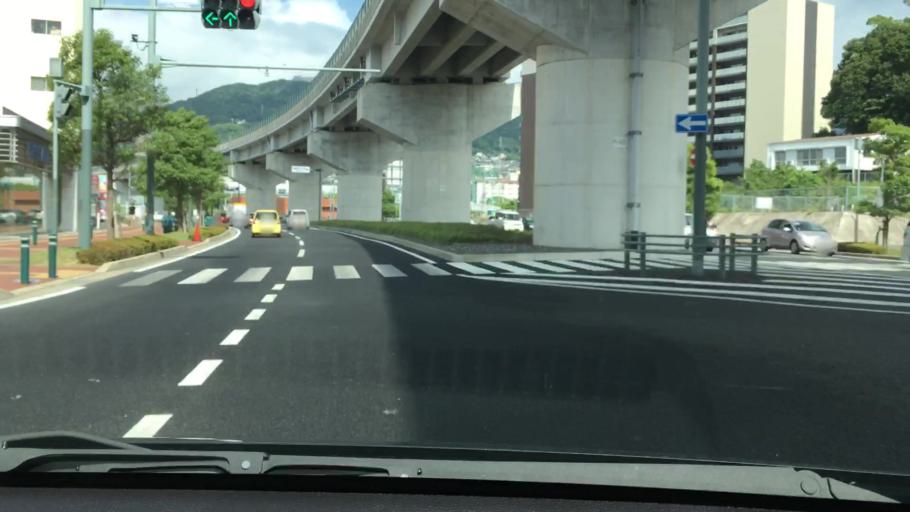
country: JP
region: Nagasaki
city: Sasebo
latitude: 33.1676
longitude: 129.7205
